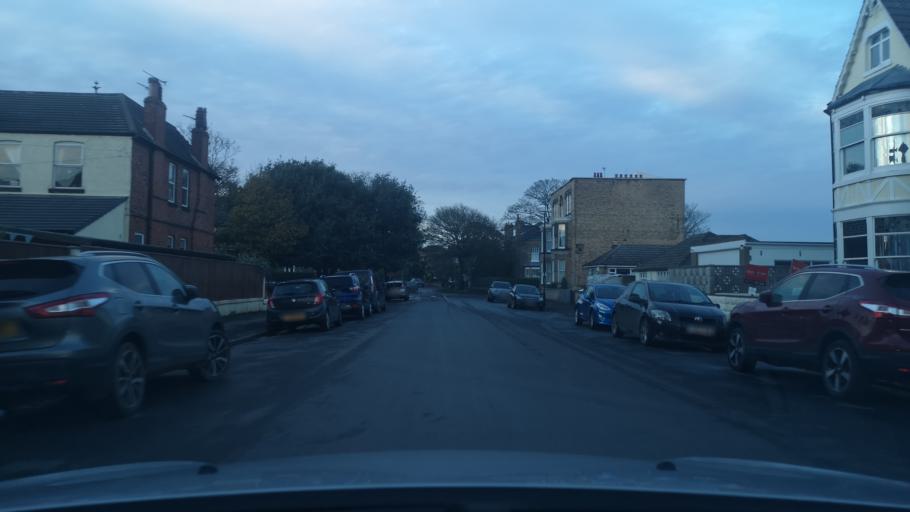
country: GB
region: England
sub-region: East Riding of Yorkshire
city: Hornsea
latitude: 53.9120
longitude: -0.1637
